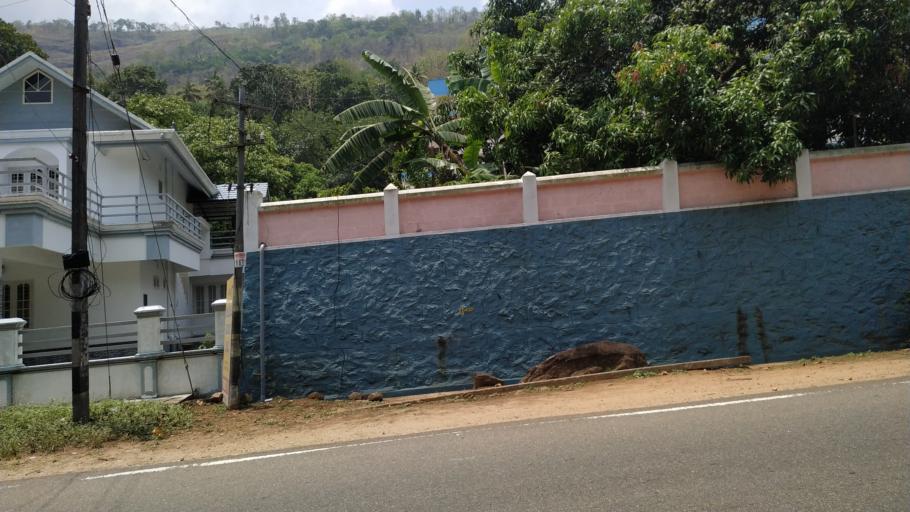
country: IN
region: Kerala
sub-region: Kottayam
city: Lalam
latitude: 9.8349
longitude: 76.7559
